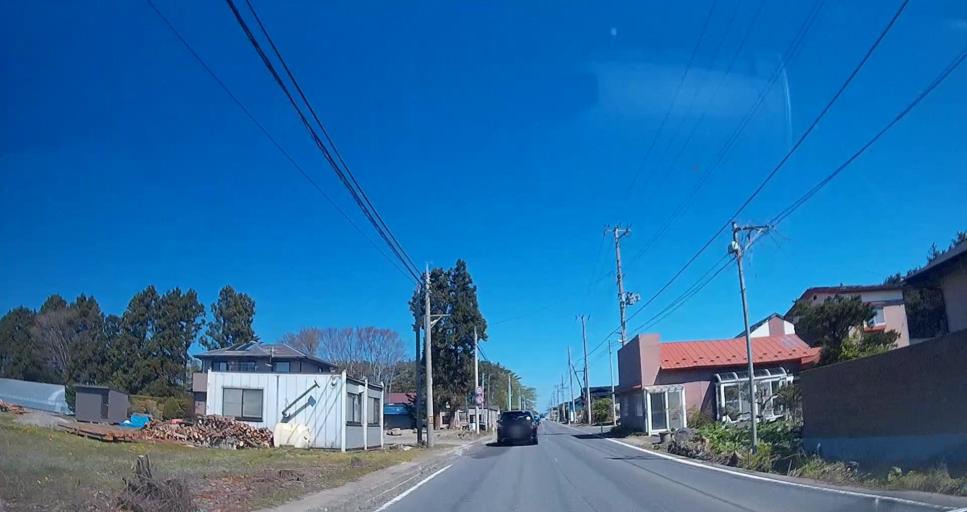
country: JP
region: Aomori
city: Misawa
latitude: 40.6773
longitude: 141.4296
